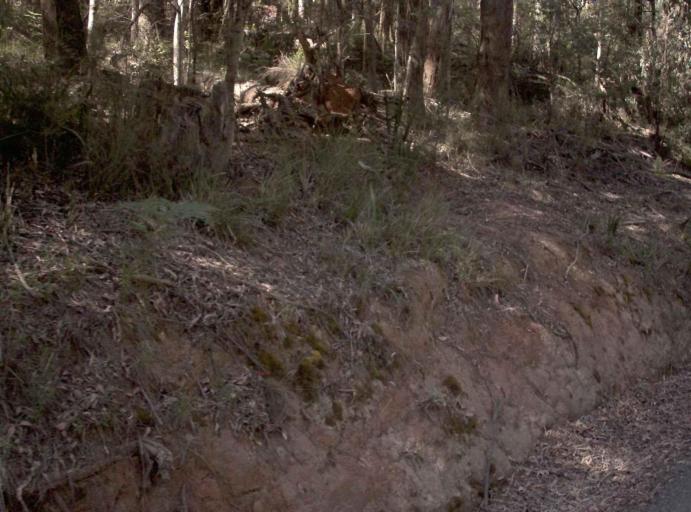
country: AU
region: New South Wales
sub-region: Bombala
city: Bombala
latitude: -37.2090
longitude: 148.7341
